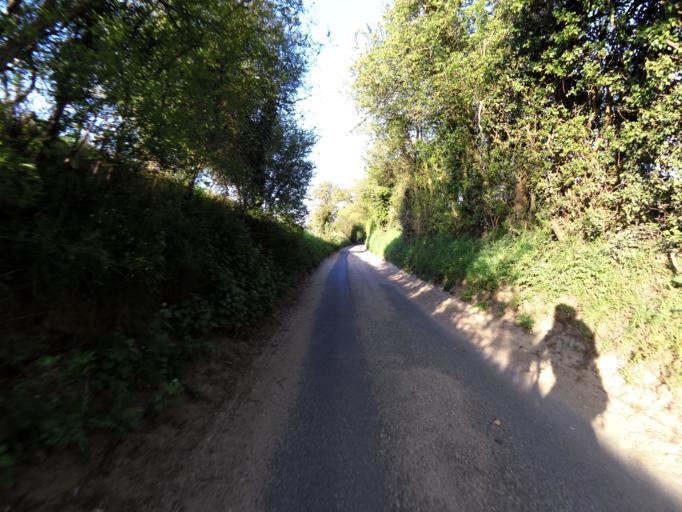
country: GB
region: England
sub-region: Suffolk
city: Capel Saint Mary
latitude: 52.0346
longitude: 1.0730
